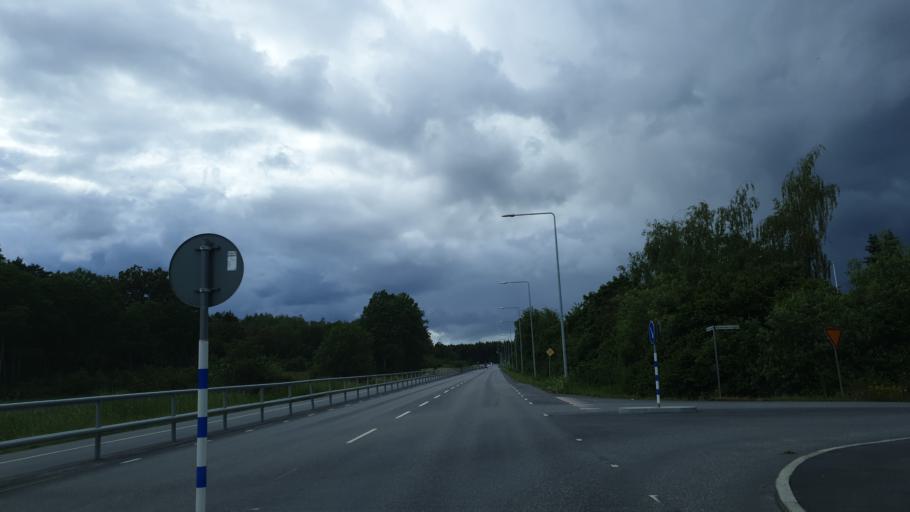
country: SE
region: Stockholm
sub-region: Jarfalla Kommun
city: Jakobsberg
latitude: 59.4209
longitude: 17.8112
